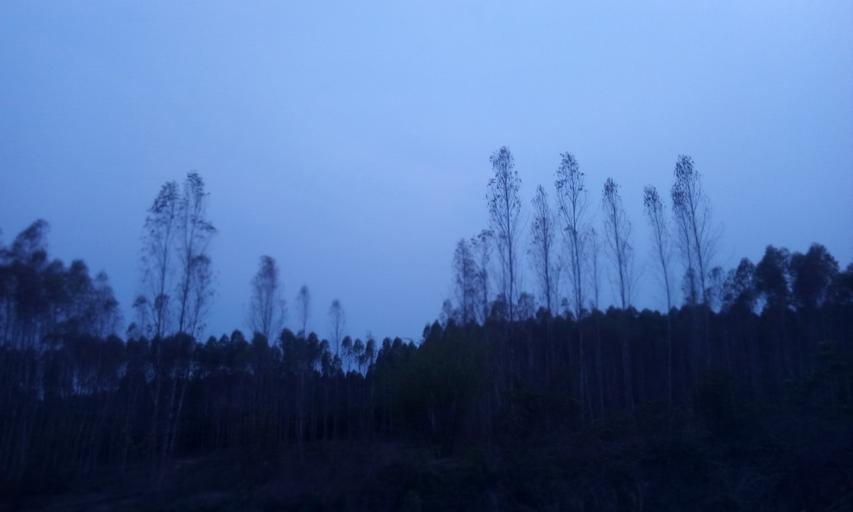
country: TH
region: Chachoengsao
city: Plaeng Yao
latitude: 13.5765
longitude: 101.2443
